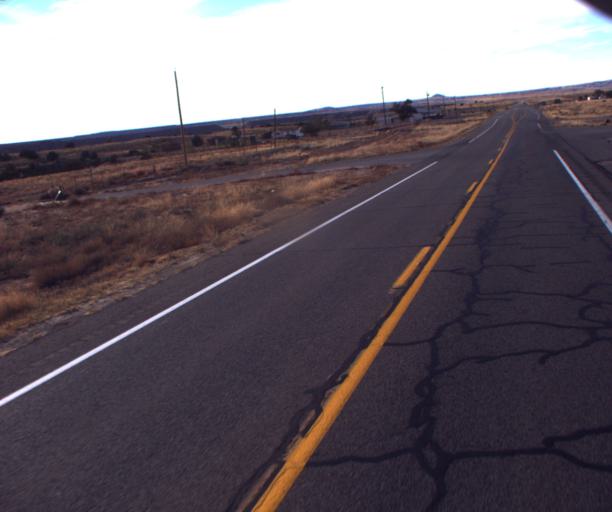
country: US
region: New Mexico
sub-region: San Juan County
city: Shiprock
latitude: 36.9190
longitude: -109.0838
